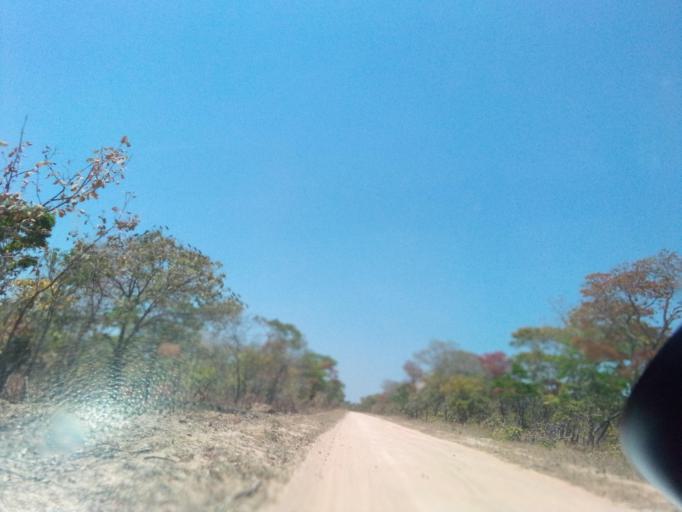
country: ZM
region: Northern
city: Mpika
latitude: -12.2366
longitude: 30.6597
